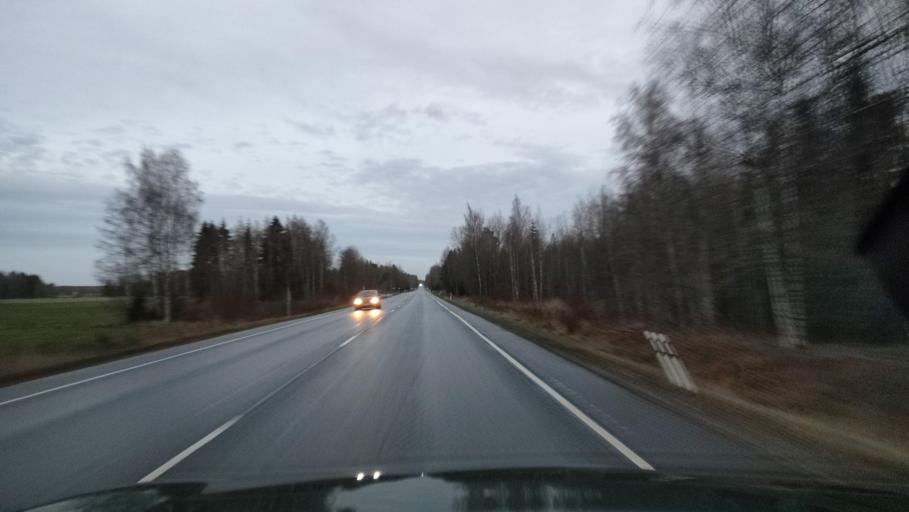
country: FI
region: Ostrobothnia
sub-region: Vaasa
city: Ristinummi
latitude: 62.9958
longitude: 21.7654
